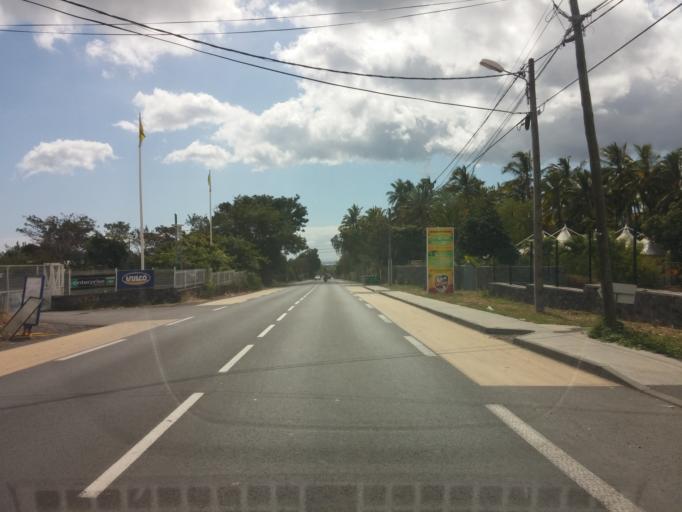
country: RE
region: Reunion
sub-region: Reunion
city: La Possession
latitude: -20.9546
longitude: 55.3240
